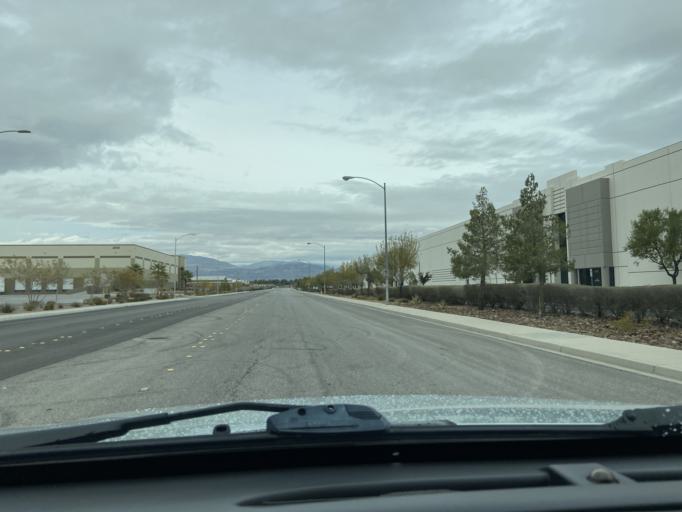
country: US
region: Nevada
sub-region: Clark County
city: North Las Vegas
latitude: 36.2447
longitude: -115.1077
